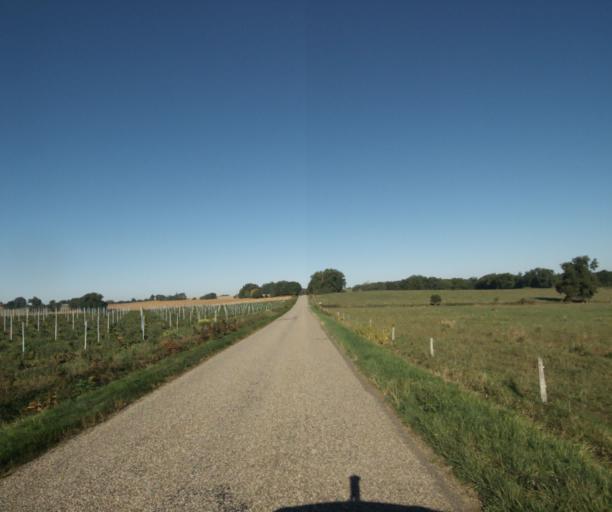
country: FR
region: Midi-Pyrenees
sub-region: Departement du Gers
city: Vic-Fezensac
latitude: 43.8234
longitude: 0.2736
